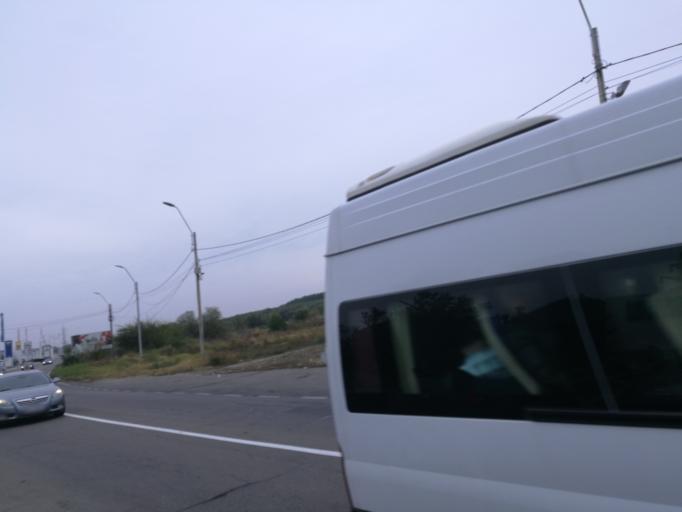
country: RO
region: Braila
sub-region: Municipiul Braila
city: Braila
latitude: 45.3003
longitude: 27.9818
